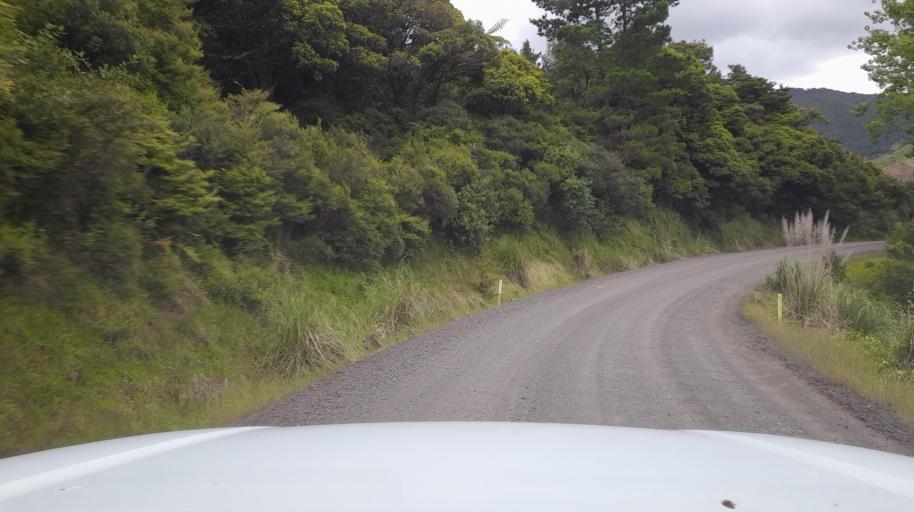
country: NZ
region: Northland
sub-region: Far North District
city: Kaitaia
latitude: -35.3238
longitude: 173.3515
